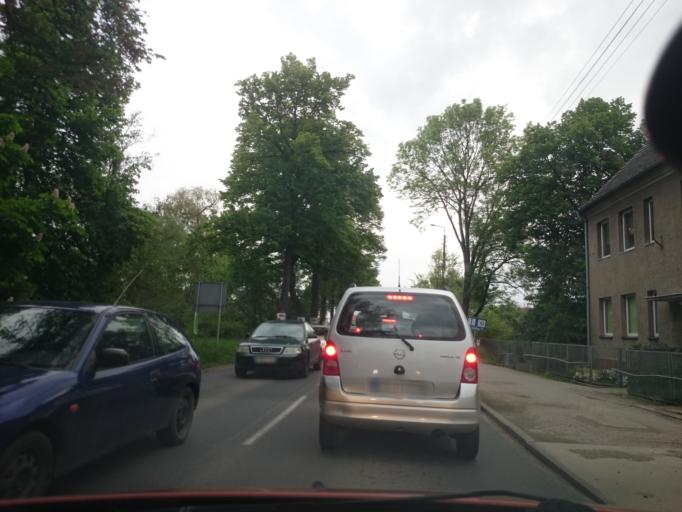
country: PL
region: Opole Voivodeship
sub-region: Powiat opolski
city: Czarnowasy
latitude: 50.7237
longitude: 17.9004
